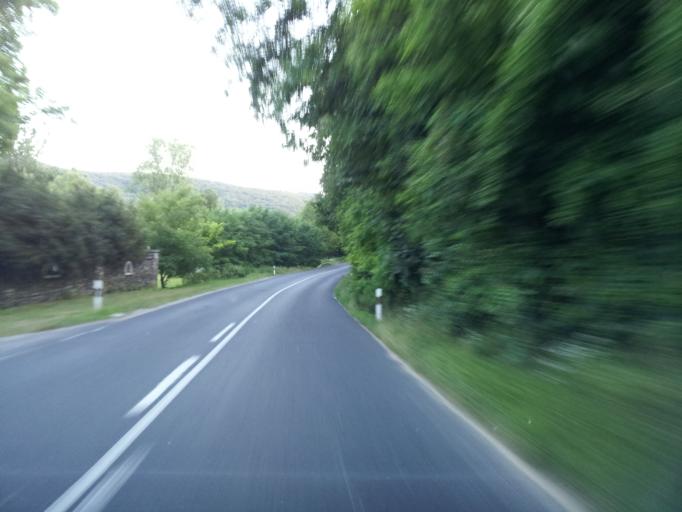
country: HU
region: Veszprem
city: Zanka
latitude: 46.9473
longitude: 17.5939
